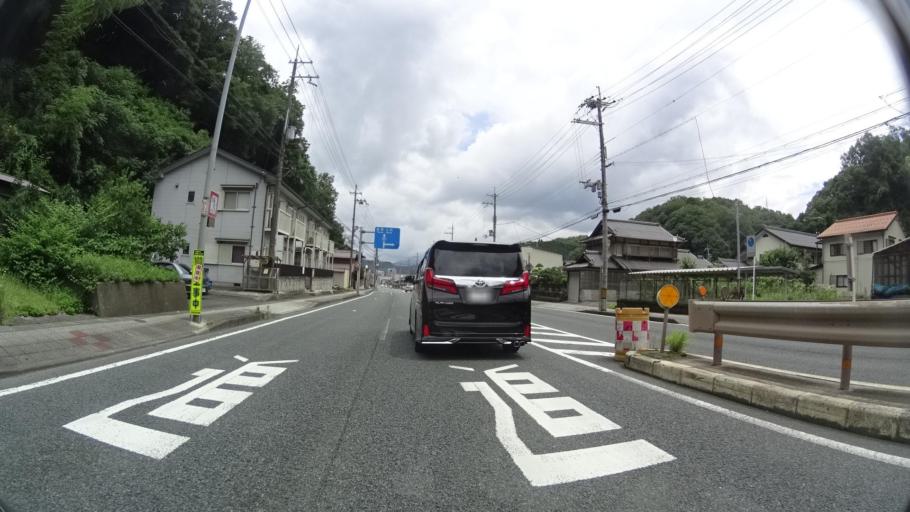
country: JP
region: Kyoto
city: Maizuru
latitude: 35.4663
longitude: 135.3637
